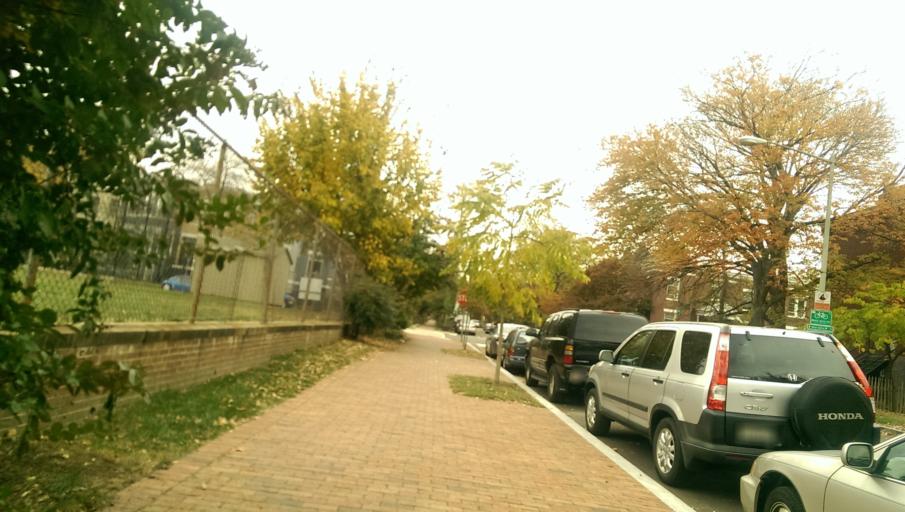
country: US
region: Washington, D.C.
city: Washington, D.C.
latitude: 38.8989
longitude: -76.9978
